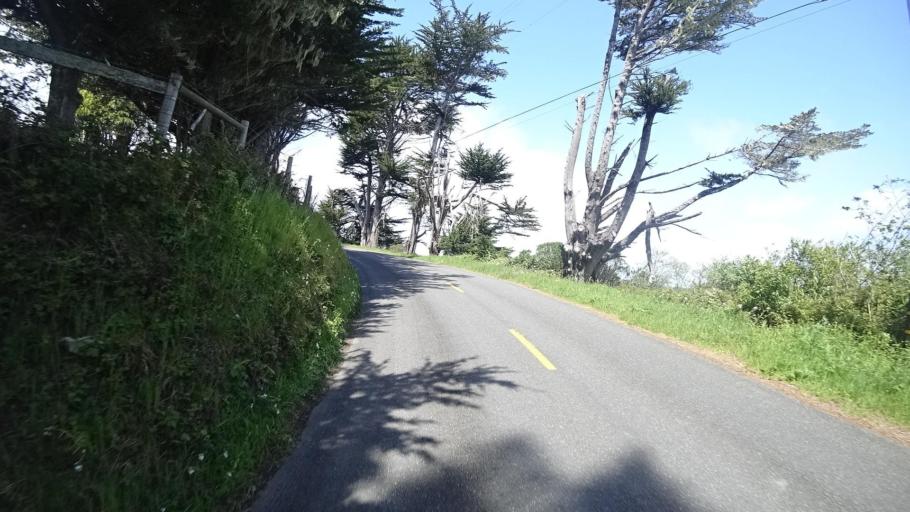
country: US
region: California
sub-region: Humboldt County
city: Humboldt Hill
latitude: 40.6745
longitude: -124.2202
